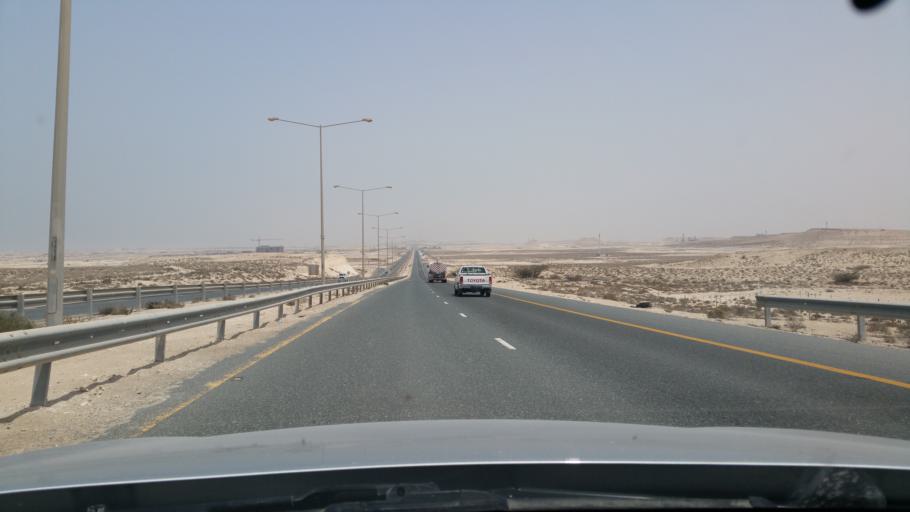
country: QA
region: Baladiyat ar Rayyan
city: Dukhan
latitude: 25.3598
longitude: 50.7793
